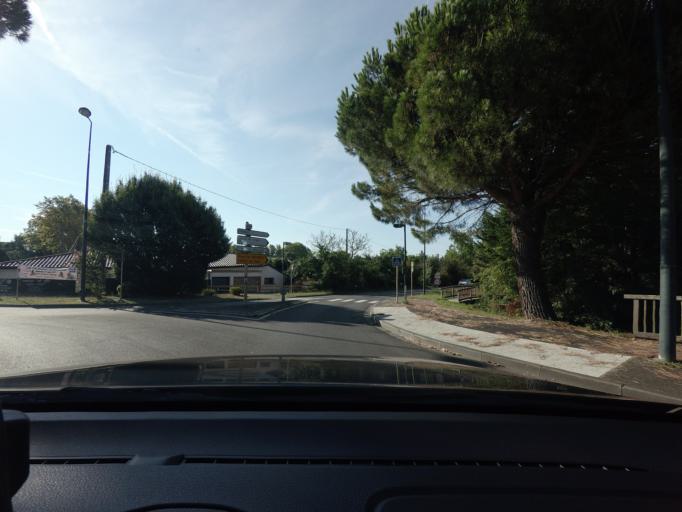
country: FR
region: Midi-Pyrenees
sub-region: Departement de la Haute-Garonne
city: Cornebarrieu
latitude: 43.6545
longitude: 1.3233
